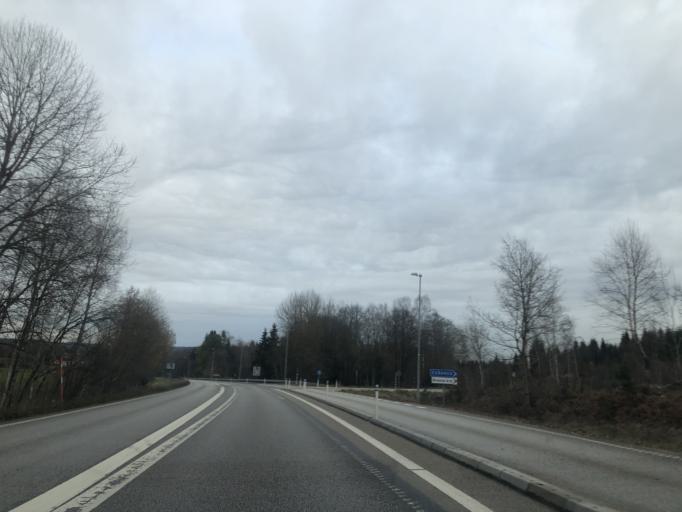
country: SE
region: Vaestra Goetaland
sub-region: Ulricehamns Kommun
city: Ulricehamn
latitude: 57.8025
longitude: 13.3401
